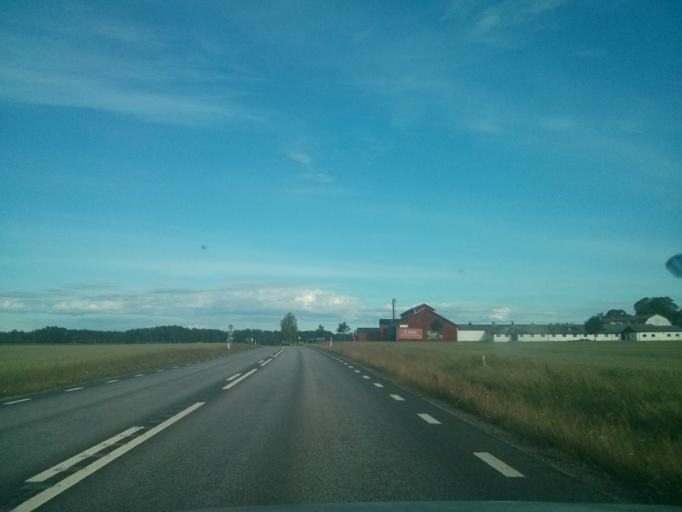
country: SE
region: Soedermanland
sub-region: Katrineholms Kommun
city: Katrineholm
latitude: 58.9681
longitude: 16.3543
